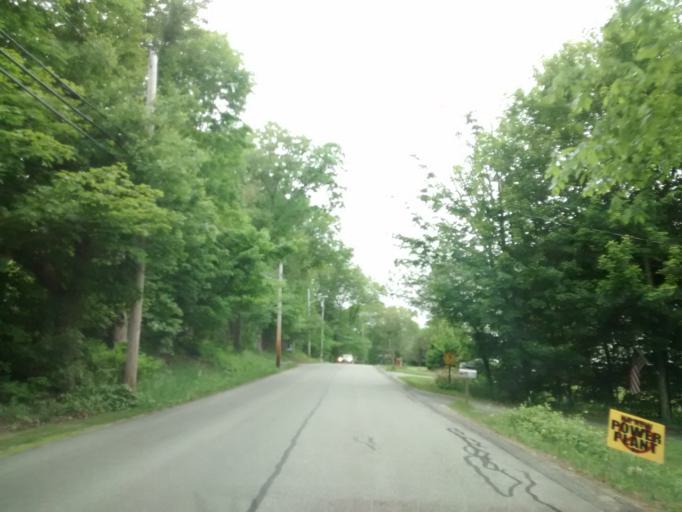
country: US
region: Rhode Island
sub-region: Providence County
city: Harrisville
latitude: 41.9592
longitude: -71.6605
